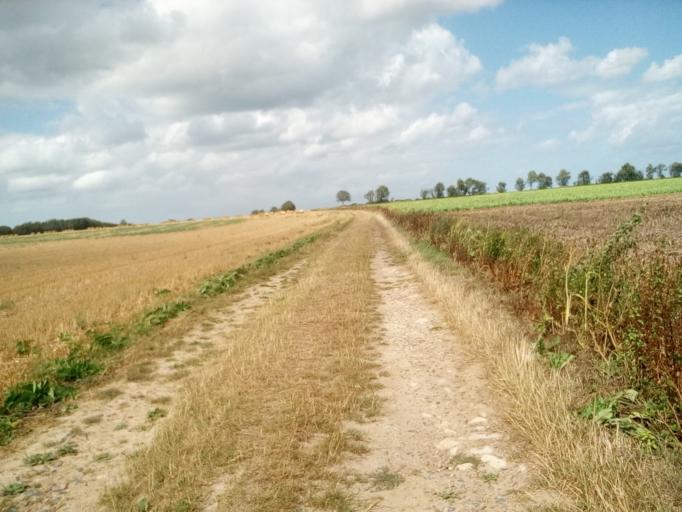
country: FR
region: Lower Normandy
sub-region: Departement du Calvados
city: Creully
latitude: 49.2934
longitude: -0.5699
